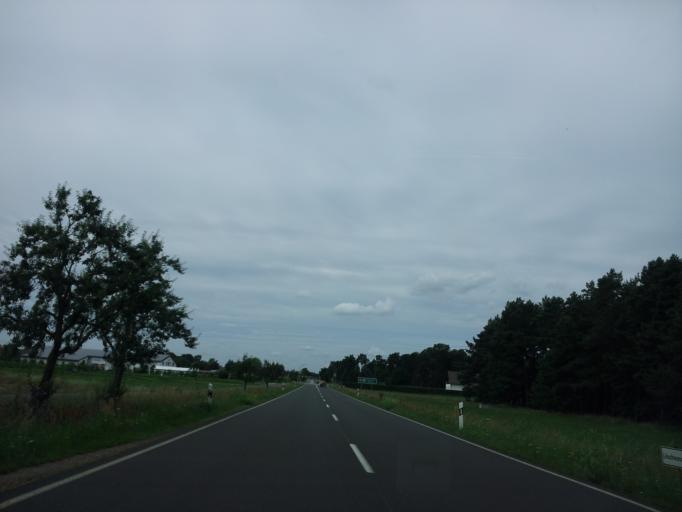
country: DE
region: Brandenburg
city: Beelitz
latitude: 52.2166
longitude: 13.0620
